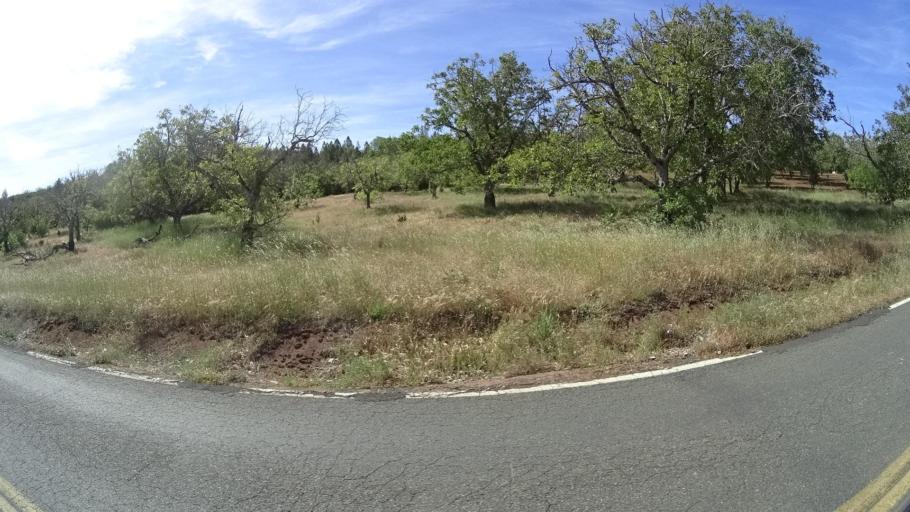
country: US
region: California
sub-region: Lake County
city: Soda Bay
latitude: 38.9129
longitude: -122.7576
